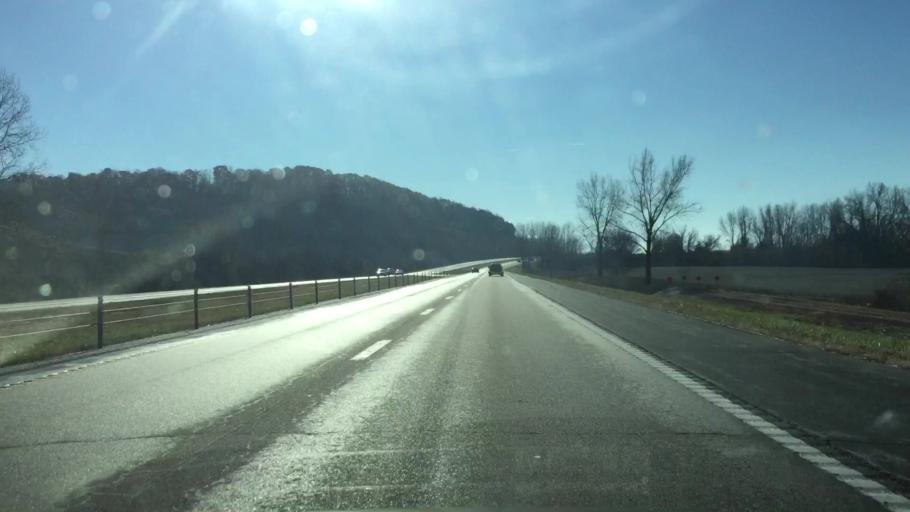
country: US
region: Missouri
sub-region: Cole County
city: Jefferson City
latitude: 38.6411
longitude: -92.1995
